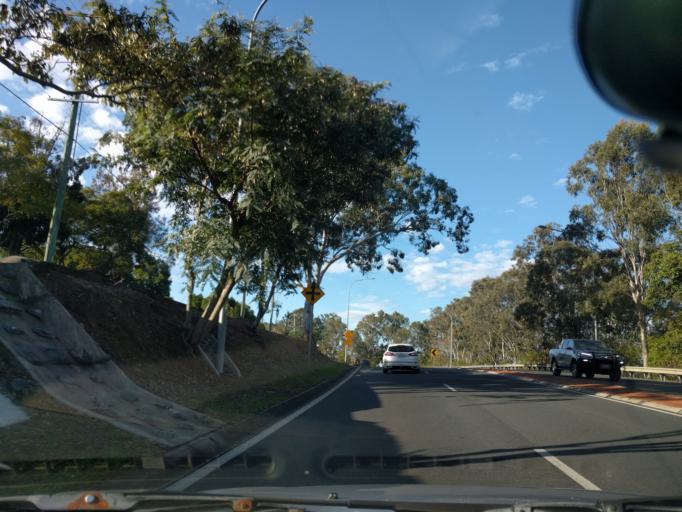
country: AU
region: Queensland
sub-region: Brisbane
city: Kenmore Hills
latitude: -27.5298
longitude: 152.9167
